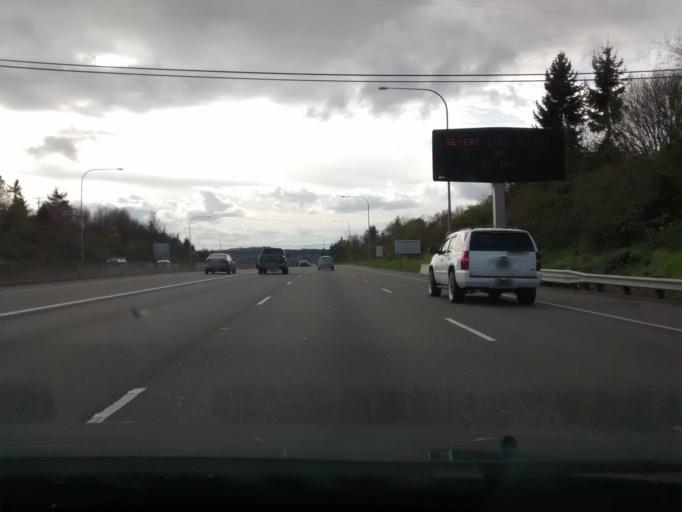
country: US
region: Washington
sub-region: Pierce County
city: Fircrest
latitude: 47.2587
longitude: -122.5258
